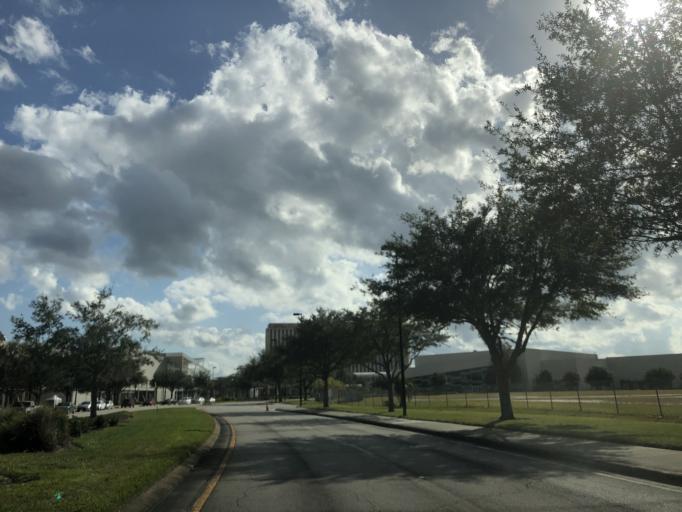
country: US
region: Florida
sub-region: Orange County
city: Williamsburg
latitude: 28.4299
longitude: -81.4648
